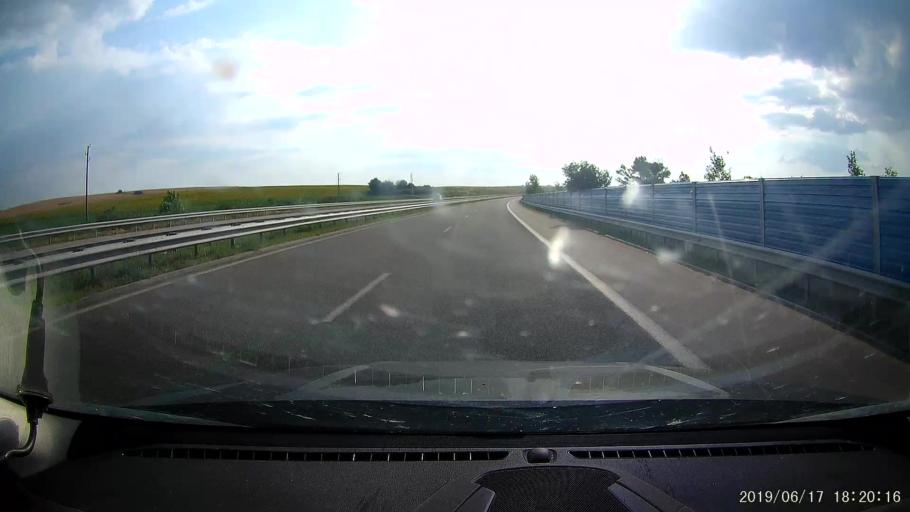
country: BG
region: Khaskovo
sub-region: Obshtina Simeonovgrad
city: Simeonovgrad
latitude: 41.9620
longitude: 25.8197
